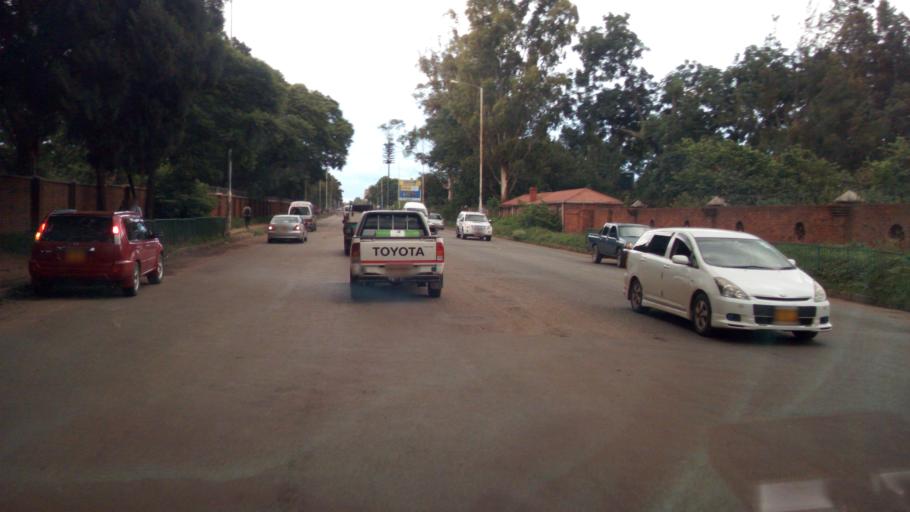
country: ZW
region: Harare
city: Harare
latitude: -17.8279
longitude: 31.0398
